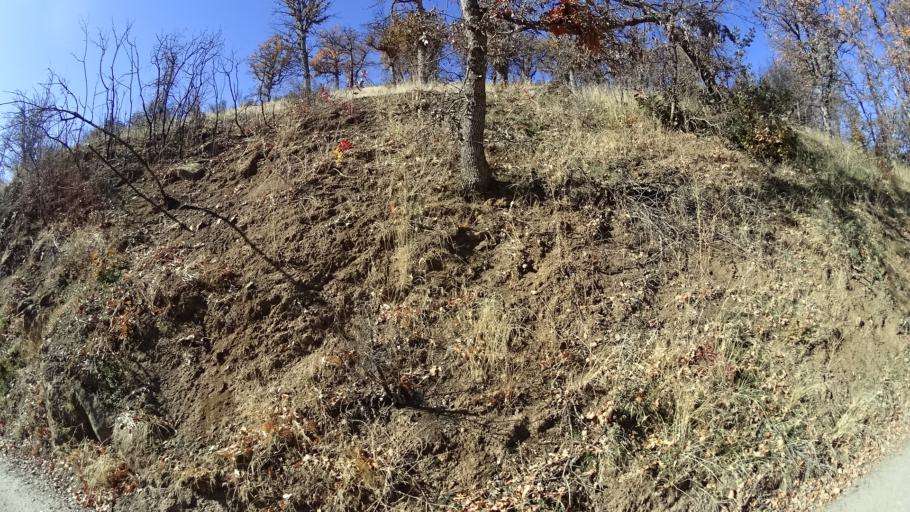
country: US
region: California
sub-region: Siskiyou County
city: Yreka
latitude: 41.9409
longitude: -122.5914
